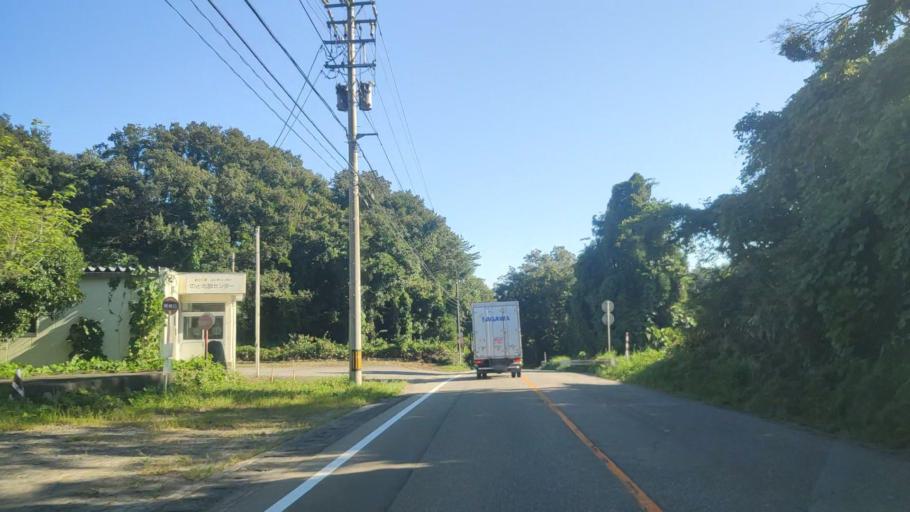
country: JP
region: Ishikawa
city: Nanao
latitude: 37.2100
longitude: 136.9081
